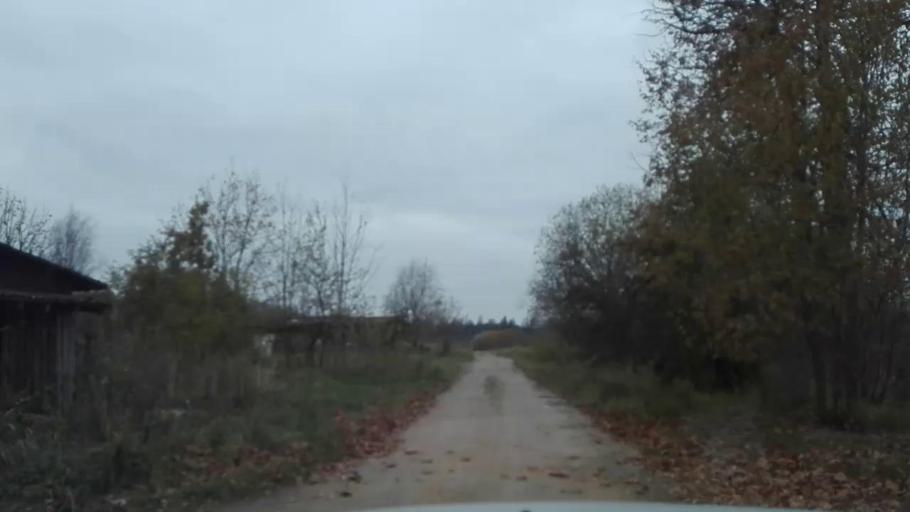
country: EE
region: Jogevamaa
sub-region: Poltsamaa linn
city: Poltsamaa
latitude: 58.4280
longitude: 26.0266
